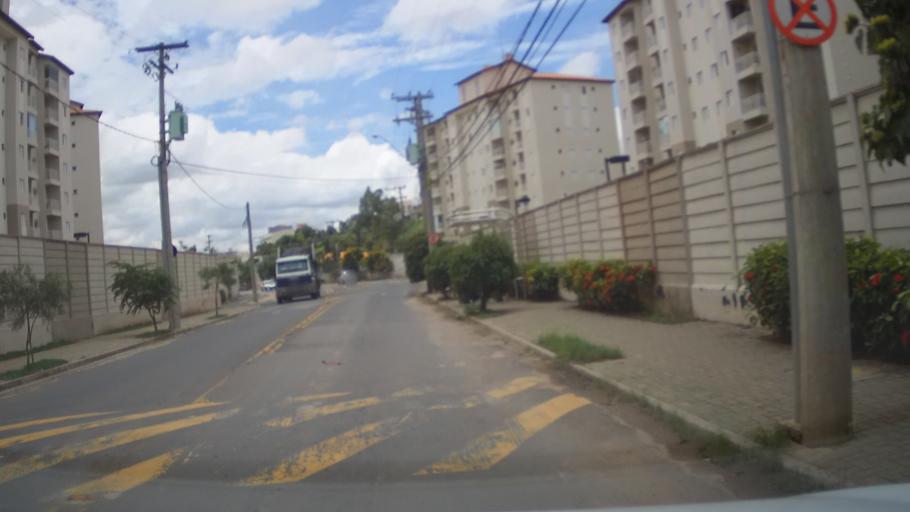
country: BR
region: Sao Paulo
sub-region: Valinhos
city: Valinhos
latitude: -22.9821
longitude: -46.9886
